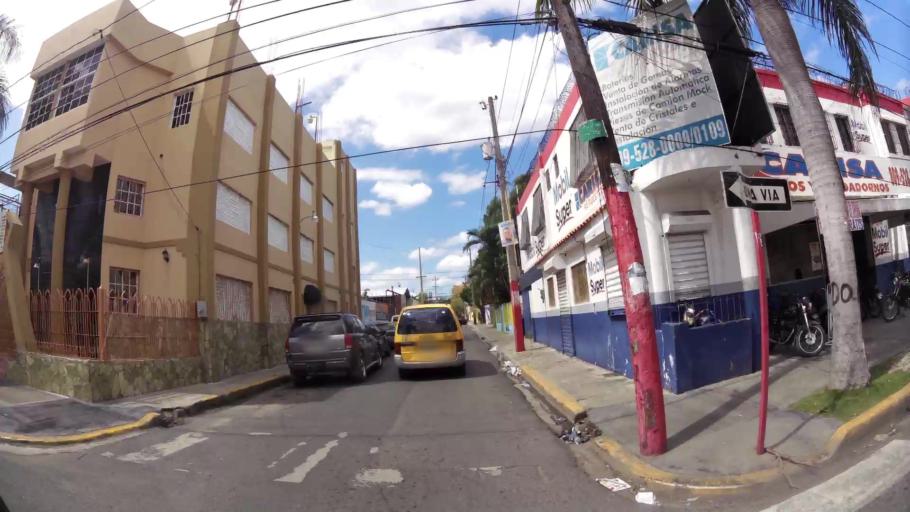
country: DO
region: San Cristobal
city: San Cristobal
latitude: 18.4192
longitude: -70.1130
